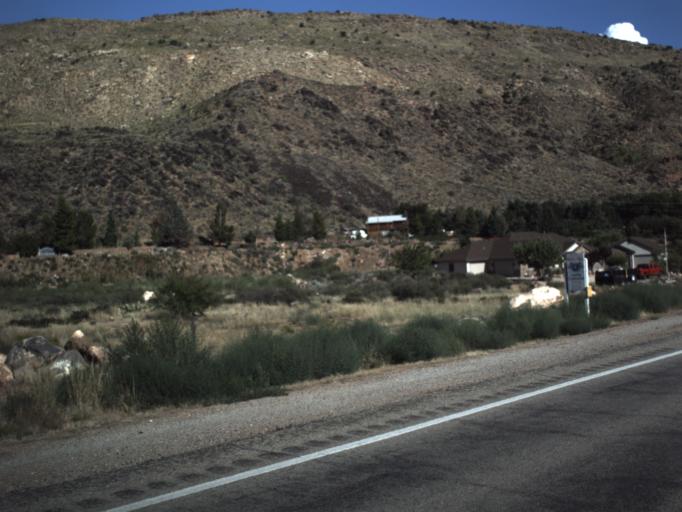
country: US
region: Utah
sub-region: Washington County
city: Toquerville
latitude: 37.2594
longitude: -113.2866
